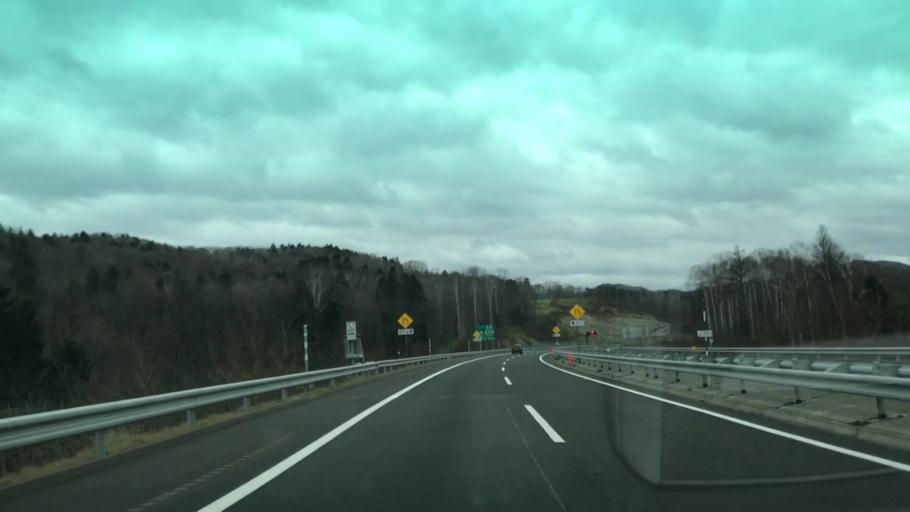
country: JP
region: Hokkaido
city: Shimo-furano
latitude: 42.9885
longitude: 142.4116
